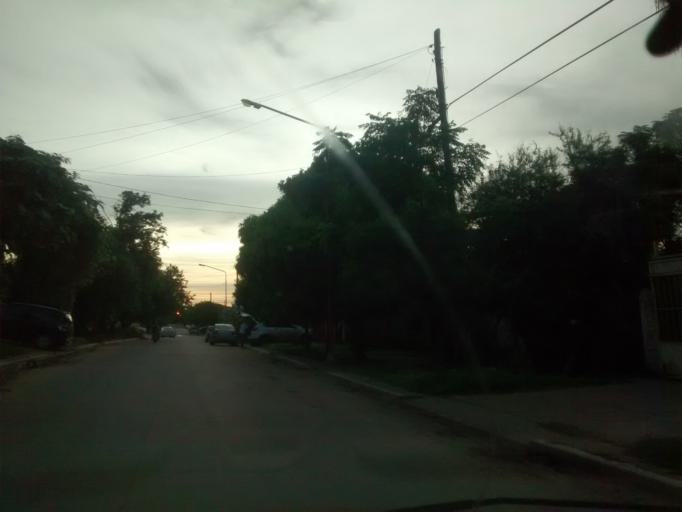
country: AR
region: Chaco
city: Resistencia
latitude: -27.4361
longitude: -58.9930
